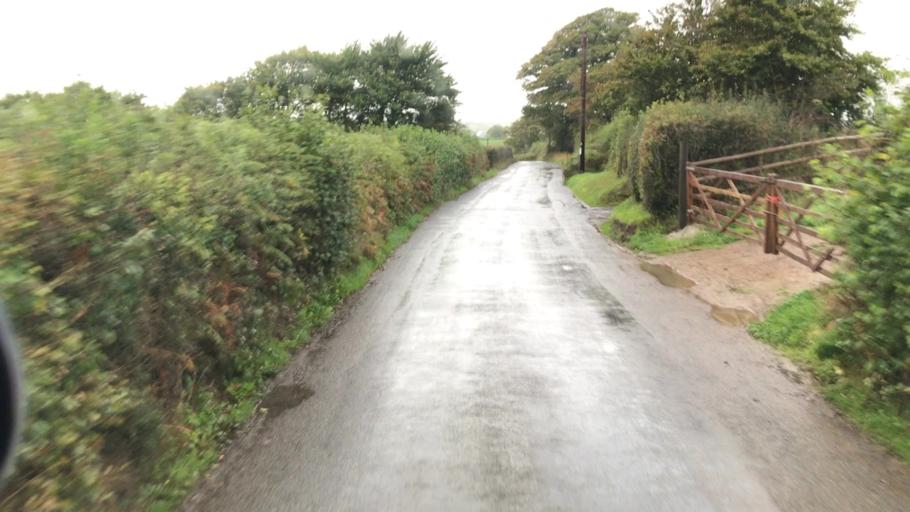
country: GB
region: England
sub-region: Devon
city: Crediton
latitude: 50.7191
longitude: -3.7329
